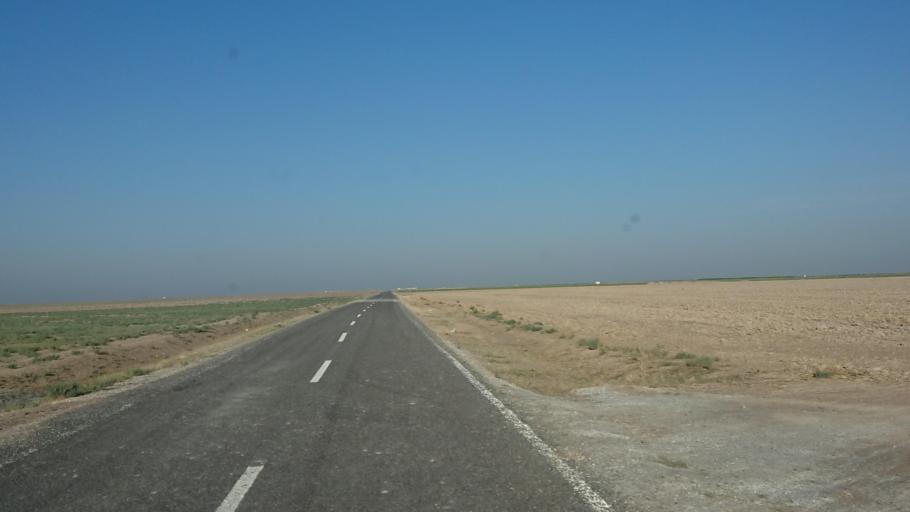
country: TR
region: Aksaray
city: Yesilova
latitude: 38.3876
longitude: 33.7843
